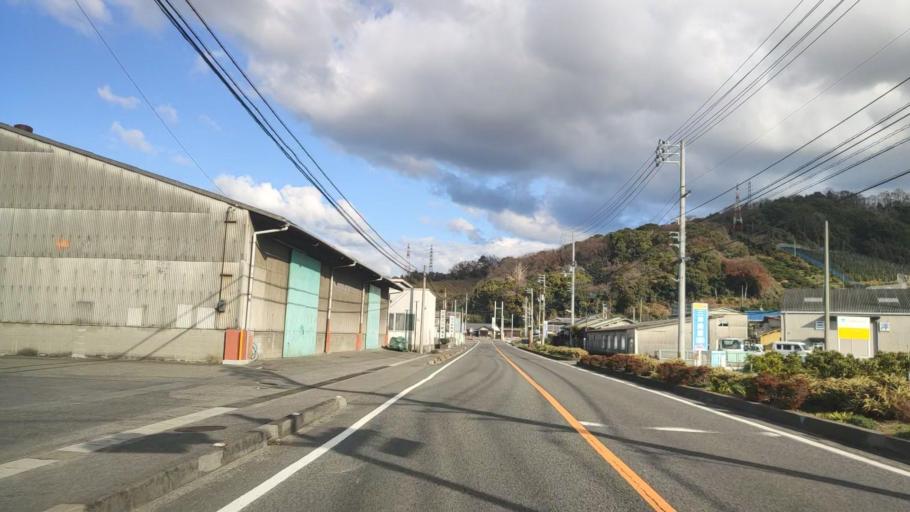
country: JP
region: Ehime
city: Masaki-cho
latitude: 33.8384
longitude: 132.7092
